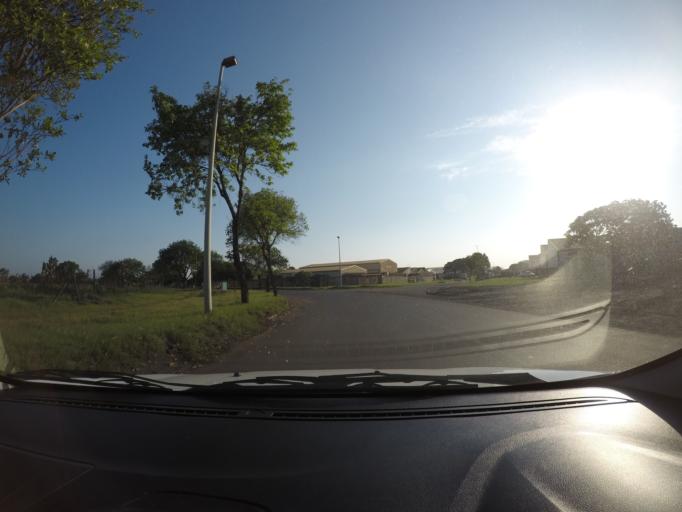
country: ZA
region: KwaZulu-Natal
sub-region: uThungulu District Municipality
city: Richards Bay
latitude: -28.7624
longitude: 32.0071
